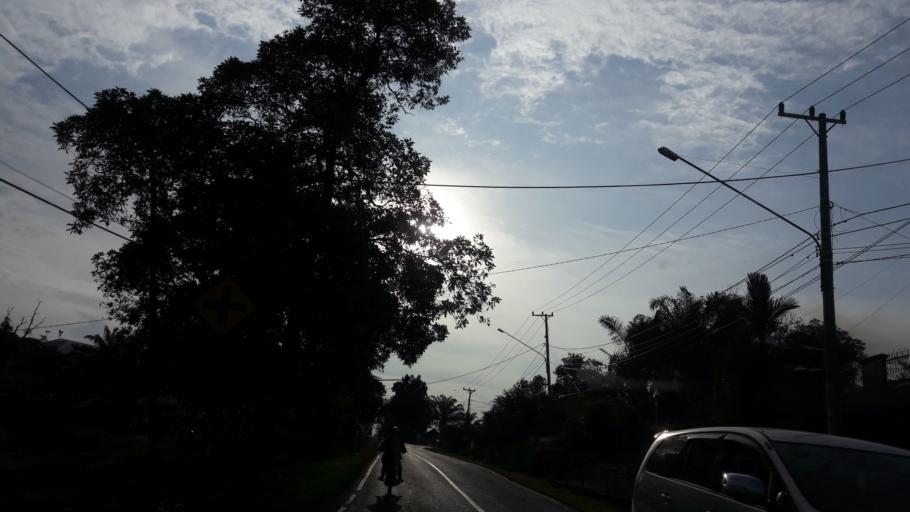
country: ID
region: South Sumatra
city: Gunungmegang Dalam
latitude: -3.2933
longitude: 103.8456
